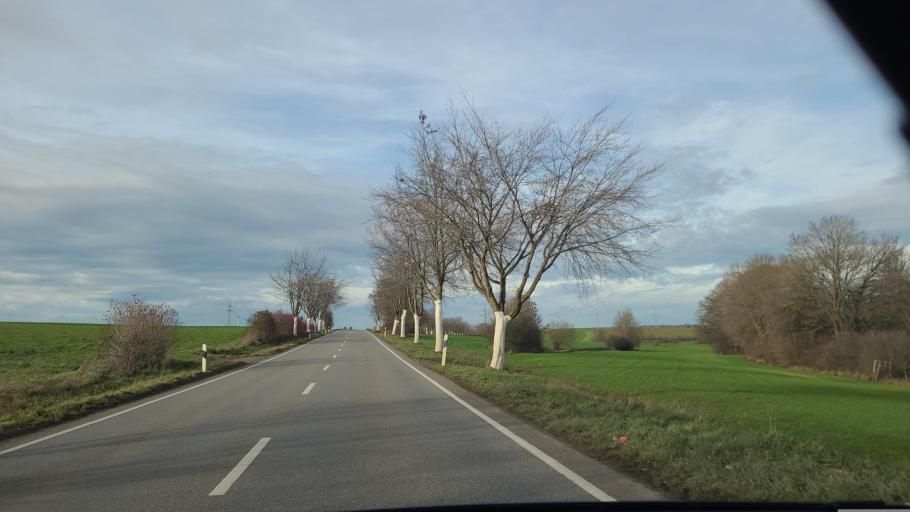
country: LU
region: Luxembourg
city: Schouweiler
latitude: 49.5906
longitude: 5.9630
